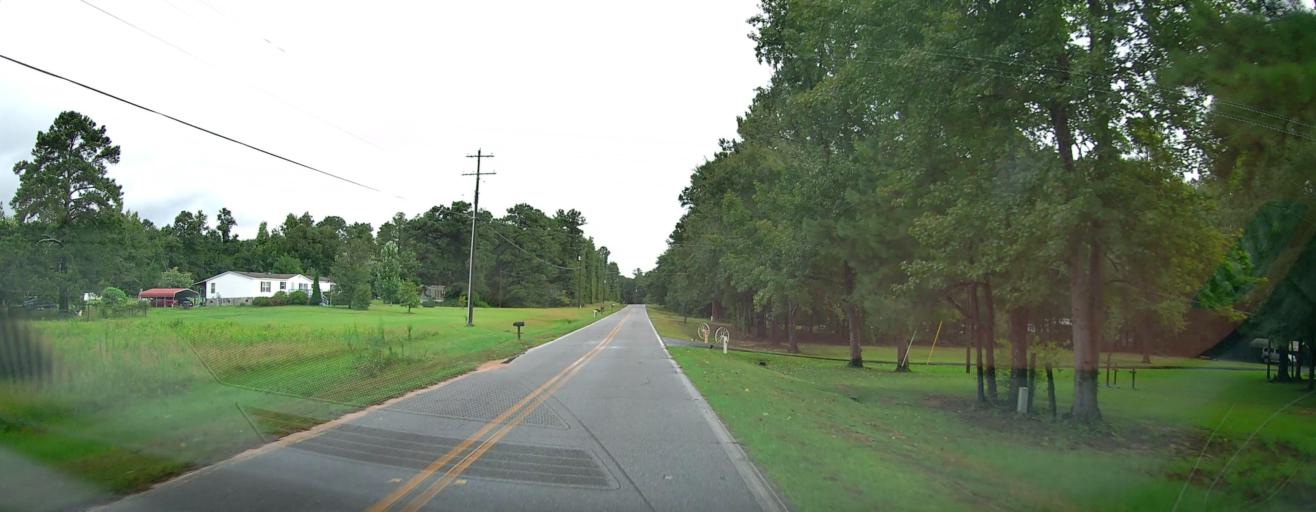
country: US
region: Georgia
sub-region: Bibb County
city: West Point
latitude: 32.7999
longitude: -83.8260
